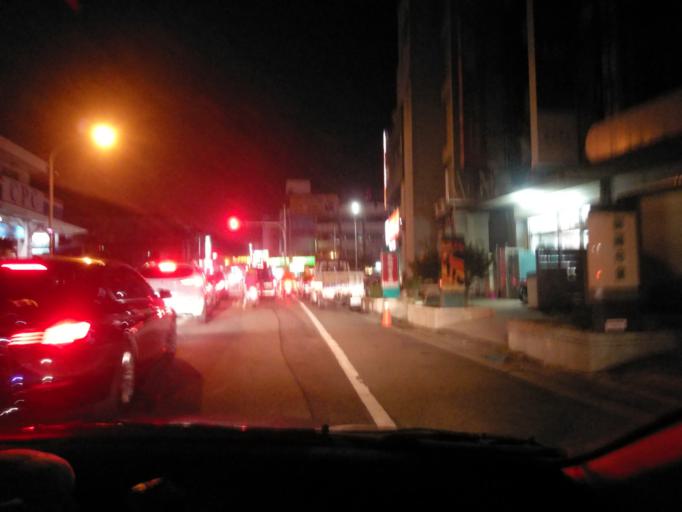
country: TW
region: Taiwan
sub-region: Miaoli
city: Miaoli
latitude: 24.6921
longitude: 120.8725
